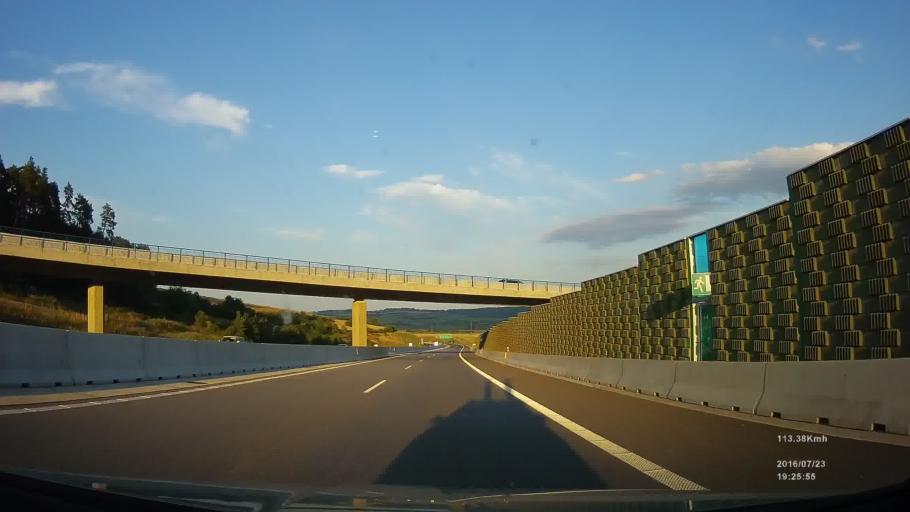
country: SK
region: Presovsky
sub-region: Okres Presov
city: Levoca
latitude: 49.0021
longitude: 20.5450
